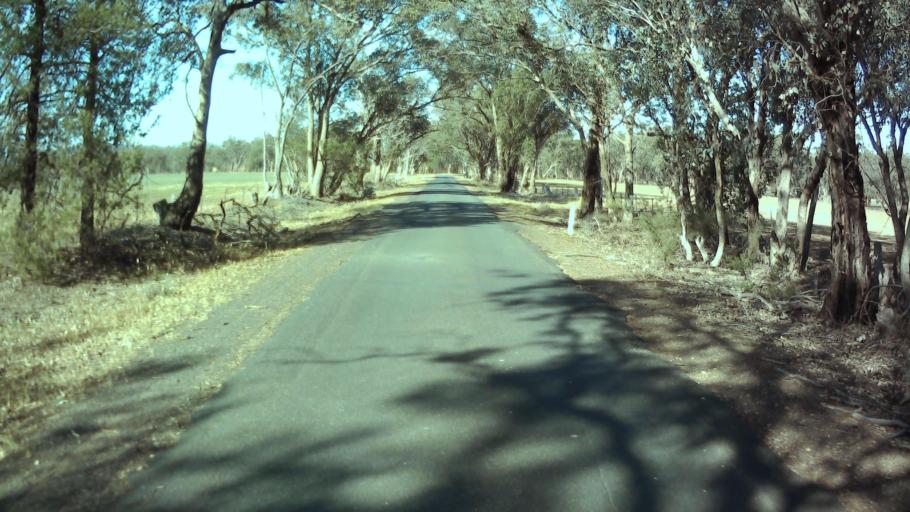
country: AU
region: New South Wales
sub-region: Weddin
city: Grenfell
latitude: -33.9060
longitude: 148.0830
